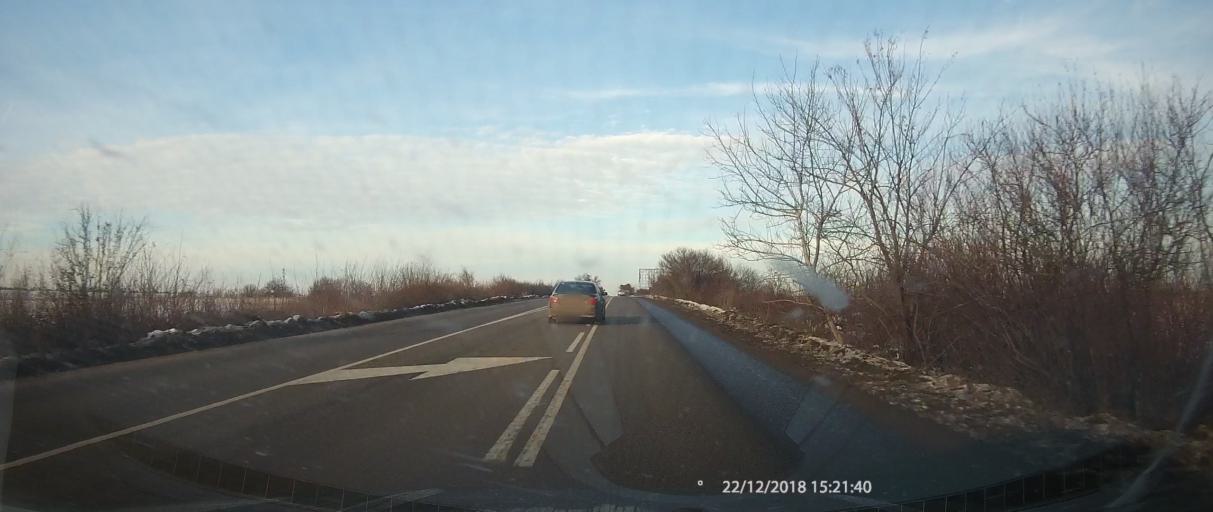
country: BG
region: Ruse
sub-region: Obshtina Ivanovo
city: Ivanovo
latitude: 43.6856
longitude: 25.9090
